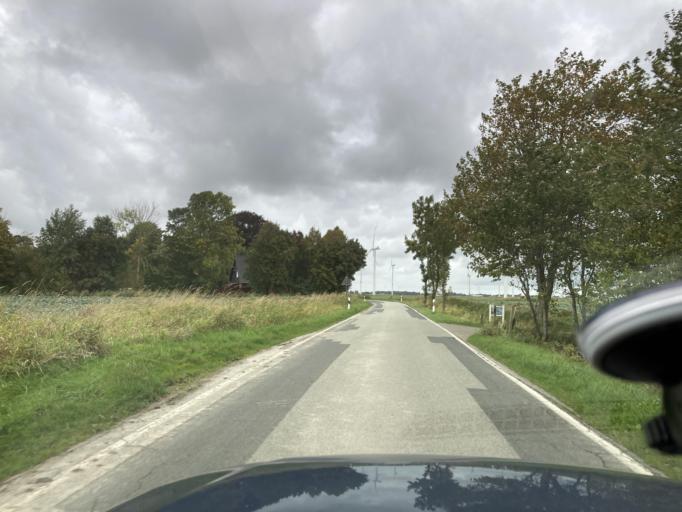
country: DE
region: Schleswig-Holstein
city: Norderwohrden
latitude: 54.1930
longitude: 9.0010
